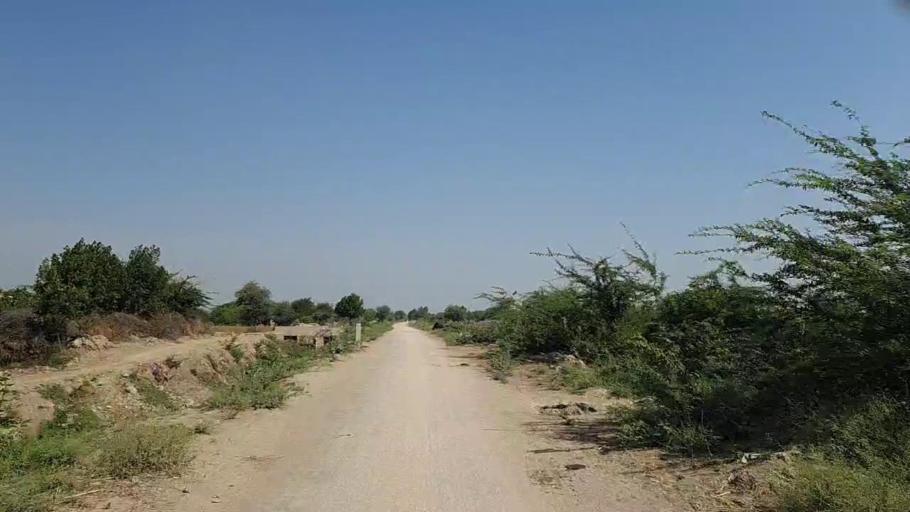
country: PK
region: Sindh
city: Mirpur Batoro
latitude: 24.6833
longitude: 68.2579
